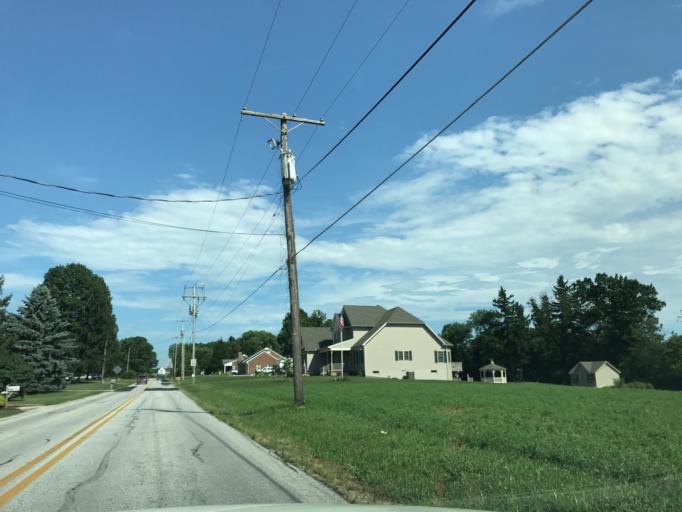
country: US
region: Pennsylvania
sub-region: York County
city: Pennville
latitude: 39.7620
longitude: -76.9926
